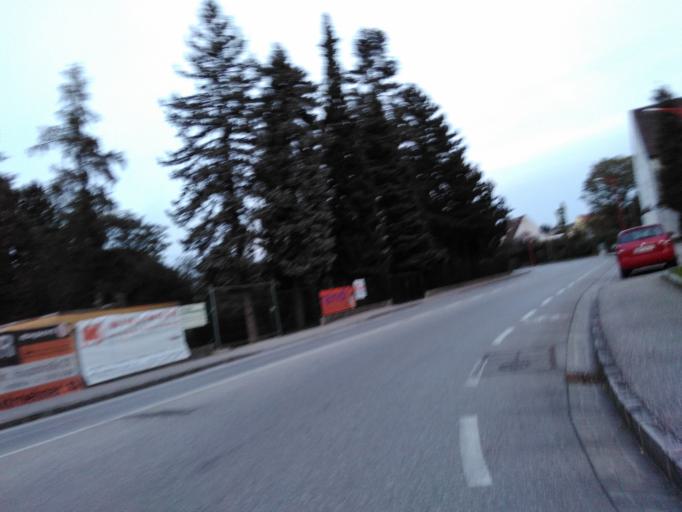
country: AT
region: Lower Austria
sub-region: Politischer Bezirk Amstetten
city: Sankt Valentin
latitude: 48.1717
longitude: 14.5125
